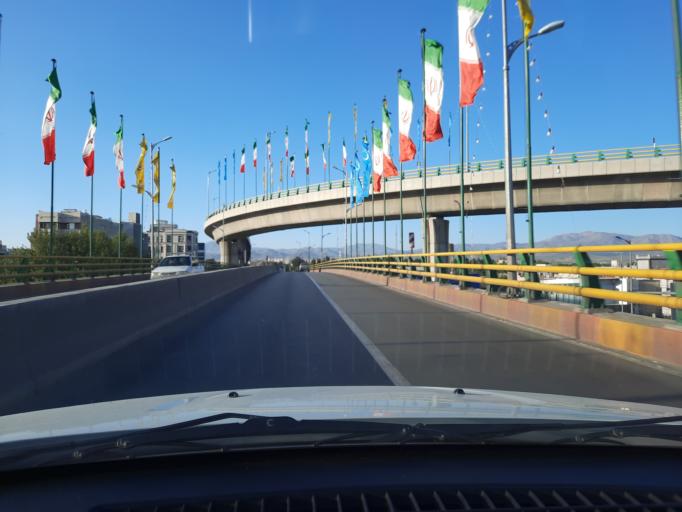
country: IR
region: Qazvin
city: Qazvin
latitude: 36.2739
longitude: 50.0236
